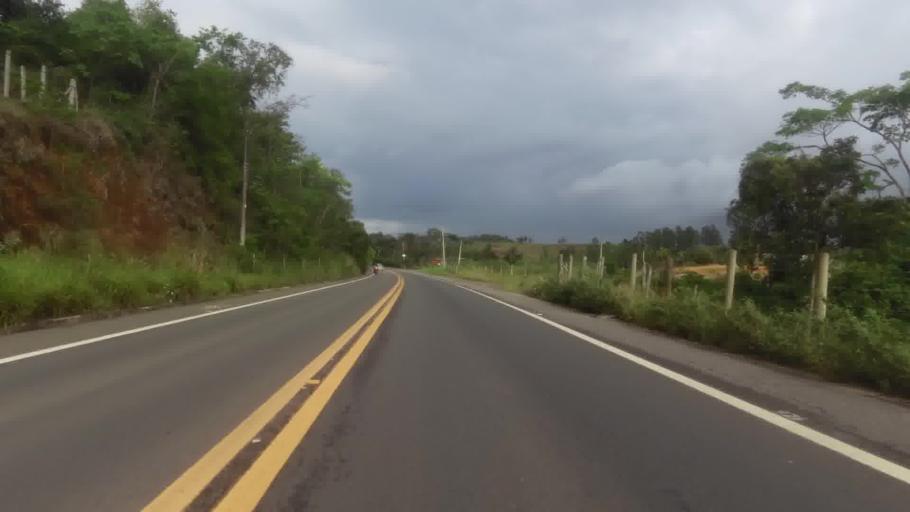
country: BR
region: Espirito Santo
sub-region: Piuma
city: Piuma
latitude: -20.8065
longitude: -40.6767
